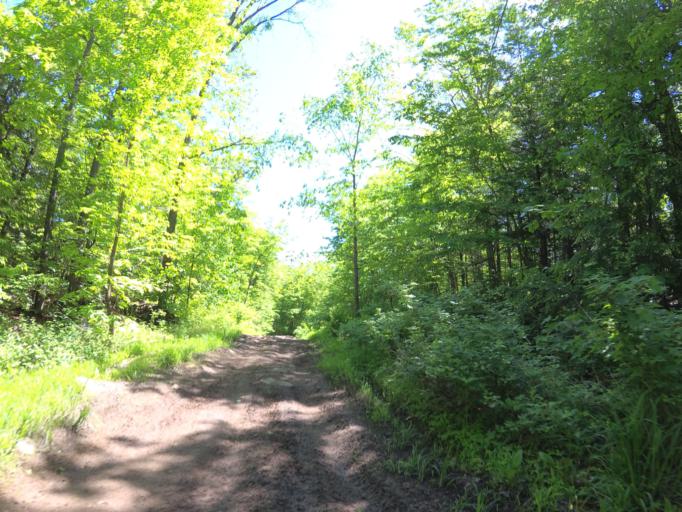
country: CA
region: Ontario
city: Renfrew
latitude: 45.0435
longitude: -77.0819
